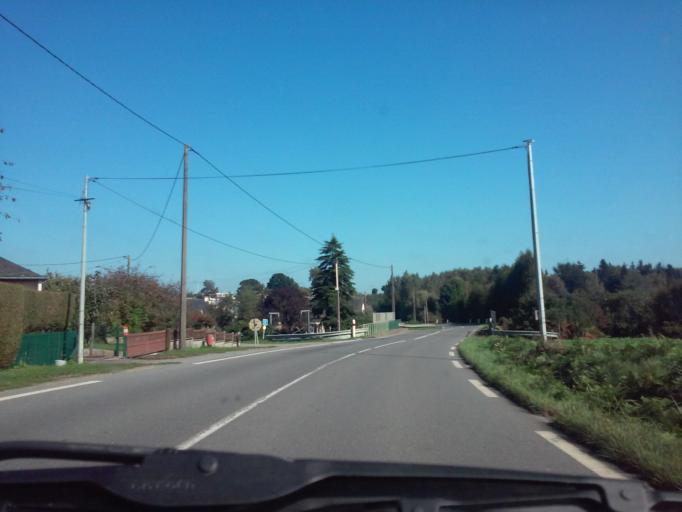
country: FR
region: Brittany
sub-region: Departement d'Ille-et-Vilaine
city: Chevaigne
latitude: 48.2051
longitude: -1.6270
